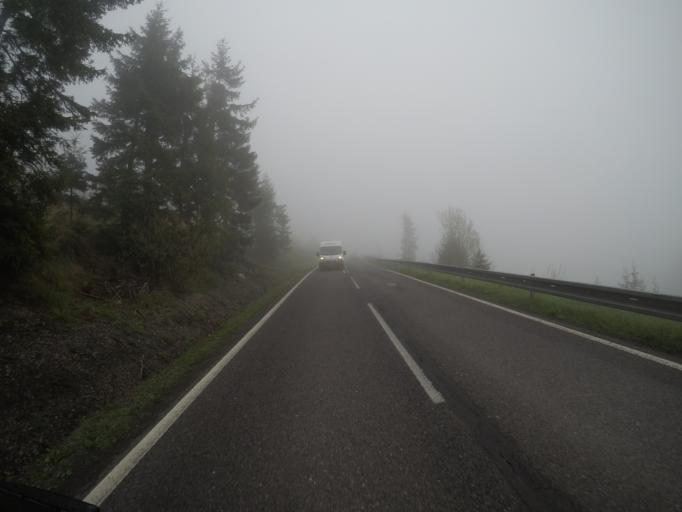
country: SK
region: Presovsky
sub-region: Okres Poprad
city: Strba
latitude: 49.1089
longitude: 20.0609
